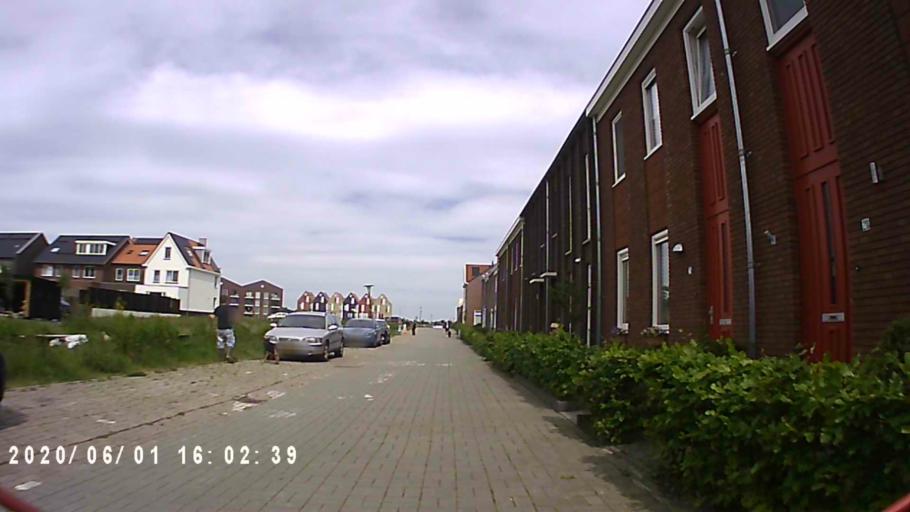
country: NL
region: Friesland
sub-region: Gemeente Leeuwarden
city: Goutum
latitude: 53.1740
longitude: 5.8190
